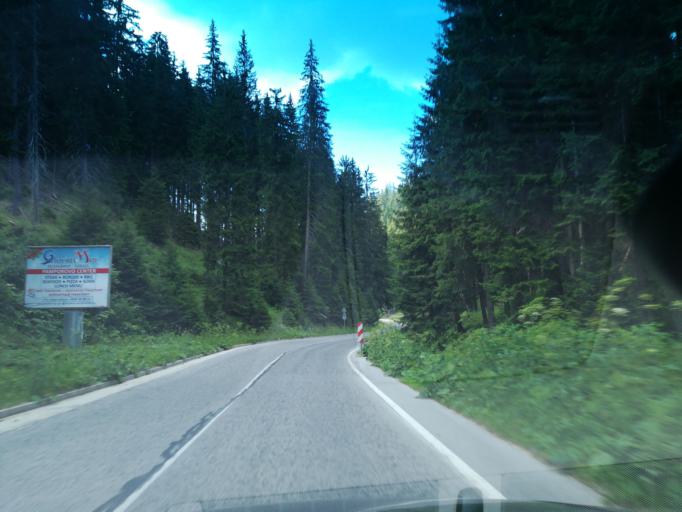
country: BG
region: Smolyan
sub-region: Obshtina Chepelare
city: Chepelare
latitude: 41.6684
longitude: 24.7146
